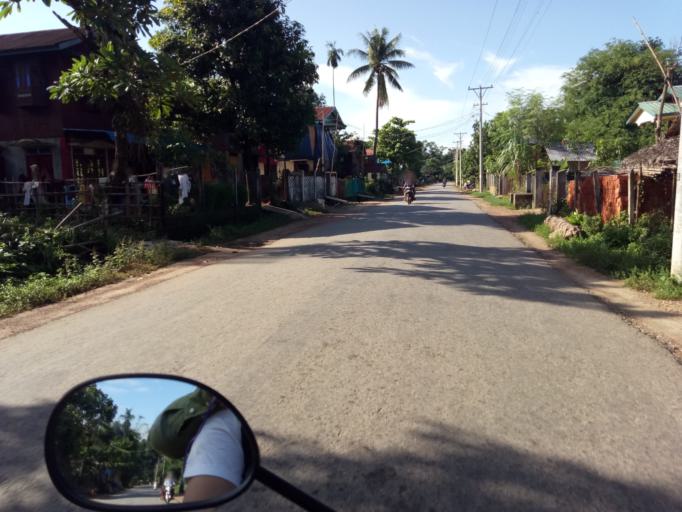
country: MM
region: Mon
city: Mawlamyine
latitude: 16.3983
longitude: 97.5552
